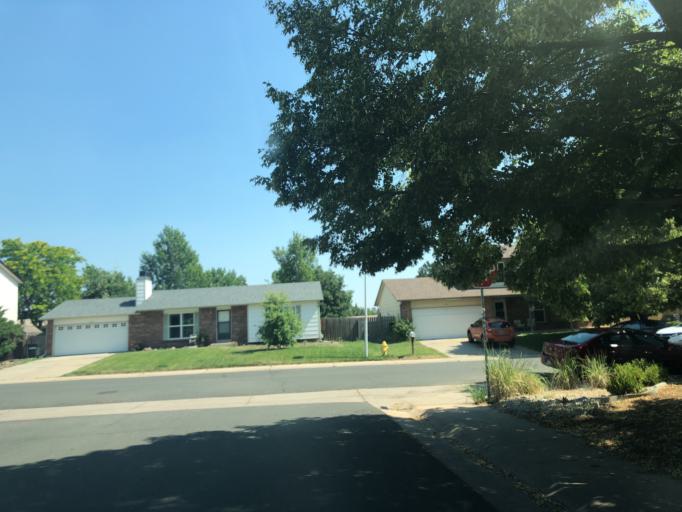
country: US
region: Colorado
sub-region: Arapahoe County
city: Dove Valley
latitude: 39.6376
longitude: -104.7671
